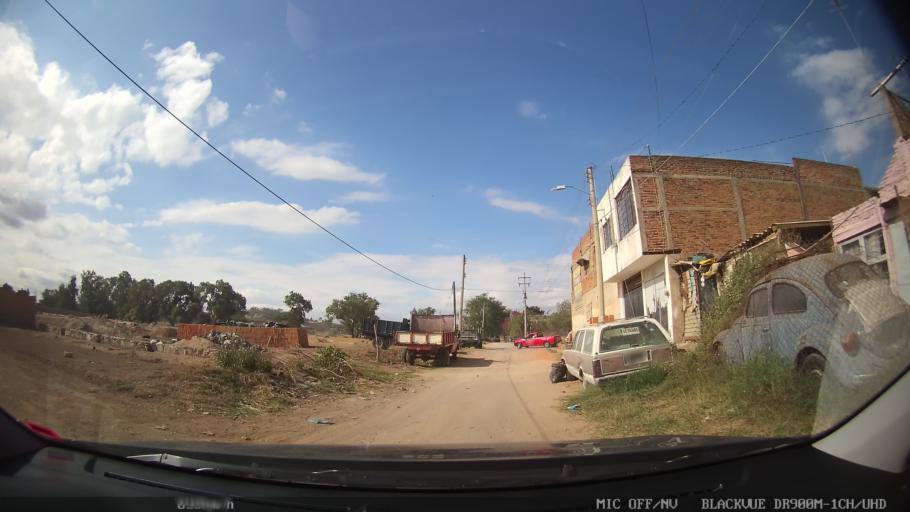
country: MX
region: Jalisco
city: Tonala
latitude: 20.6506
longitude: -103.2486
